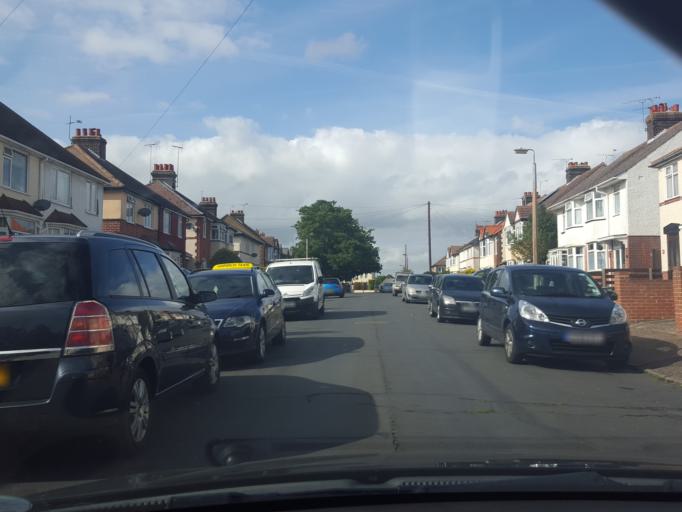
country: GB
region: England
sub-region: Essex
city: Dovercourt
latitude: 51.9334
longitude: 1.2658
